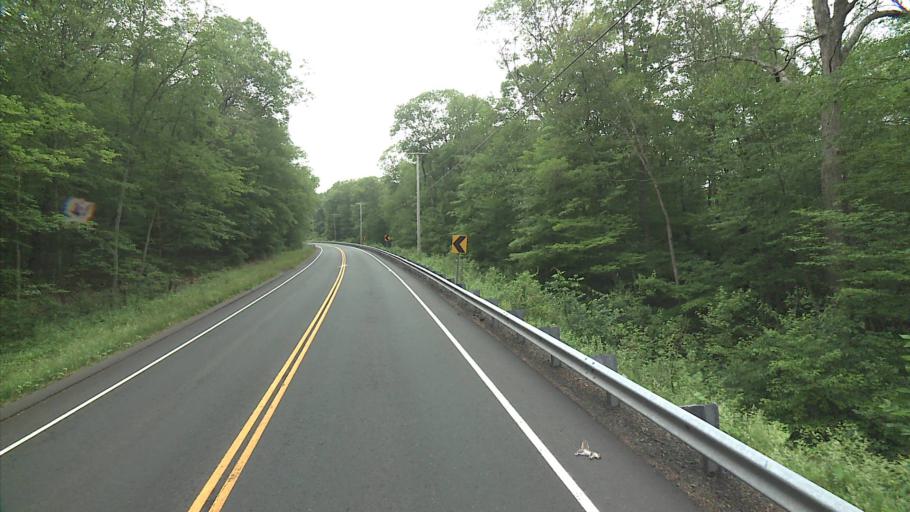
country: US
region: Connecticut
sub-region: Hartford County
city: Terramuggus
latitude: 41.6977
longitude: -72.4567
